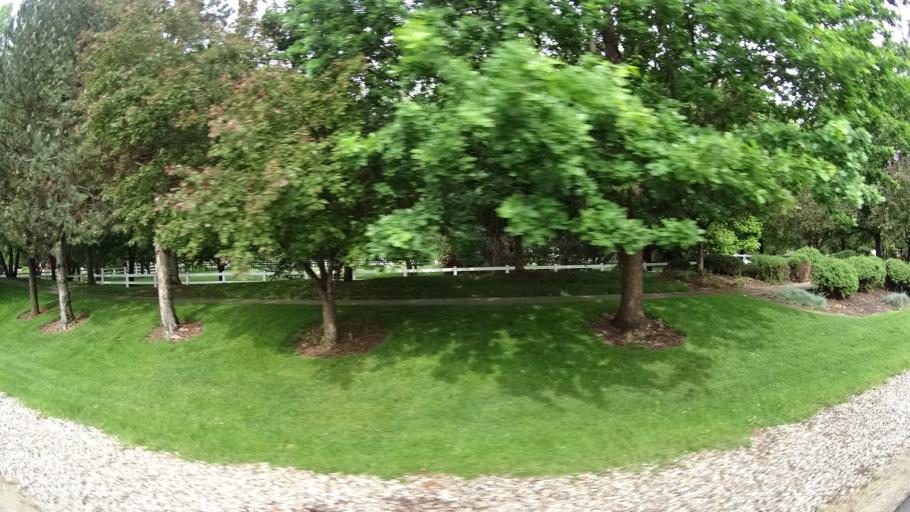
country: US
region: Idaho
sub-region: Ada County
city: Eagle
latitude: 43.7158
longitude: -116.3792
